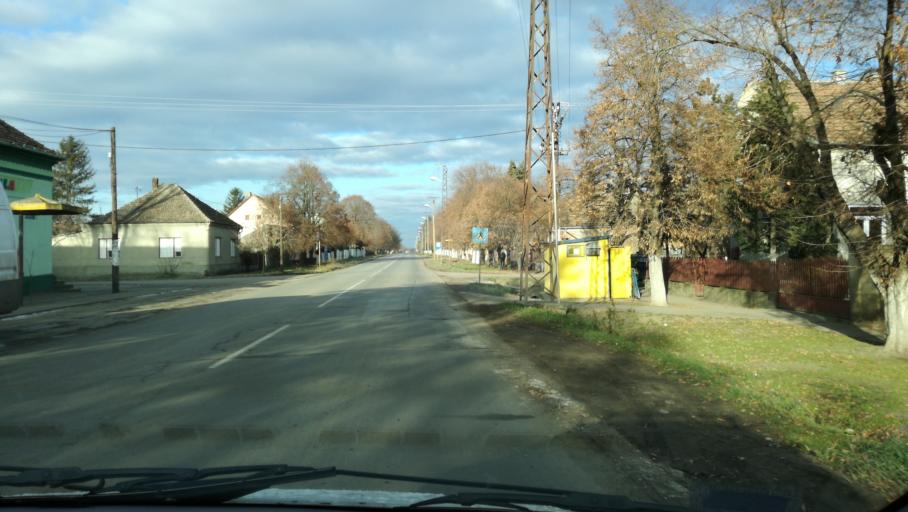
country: RS
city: Tiszahegyes
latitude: 45.8221
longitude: 20.3156
